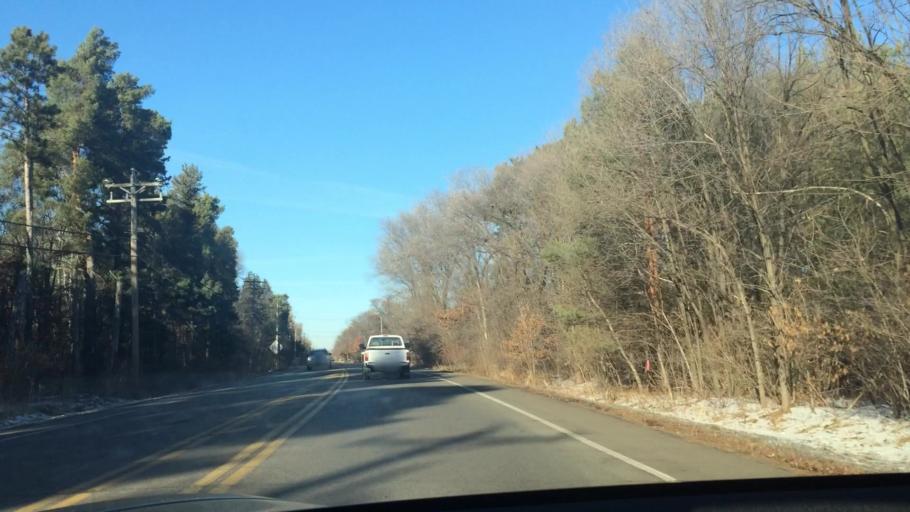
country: US
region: Minnesota
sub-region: Anoka County
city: Circle Pines
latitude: 45.1256
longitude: -93.1272
